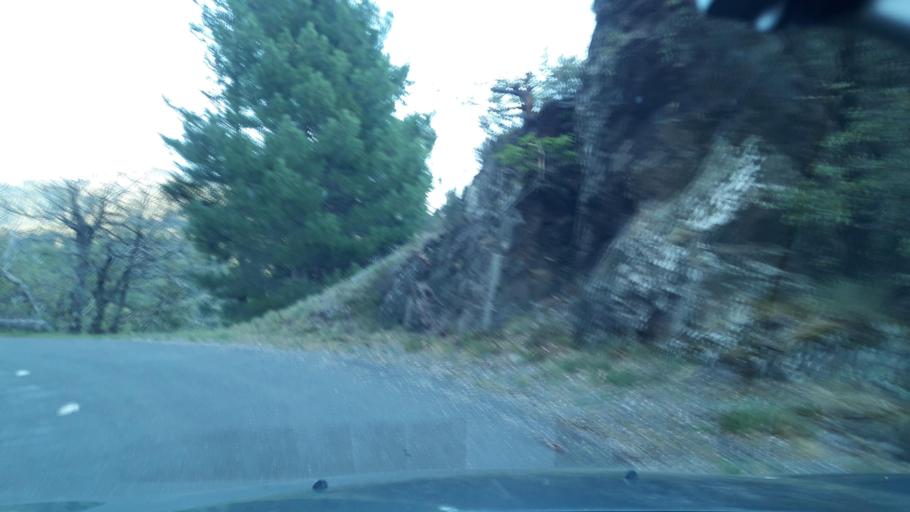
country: FR
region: Languedoc-Roussillon
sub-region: Departement du Gard
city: Valleraugue
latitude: 44.1018
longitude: 3.6493
